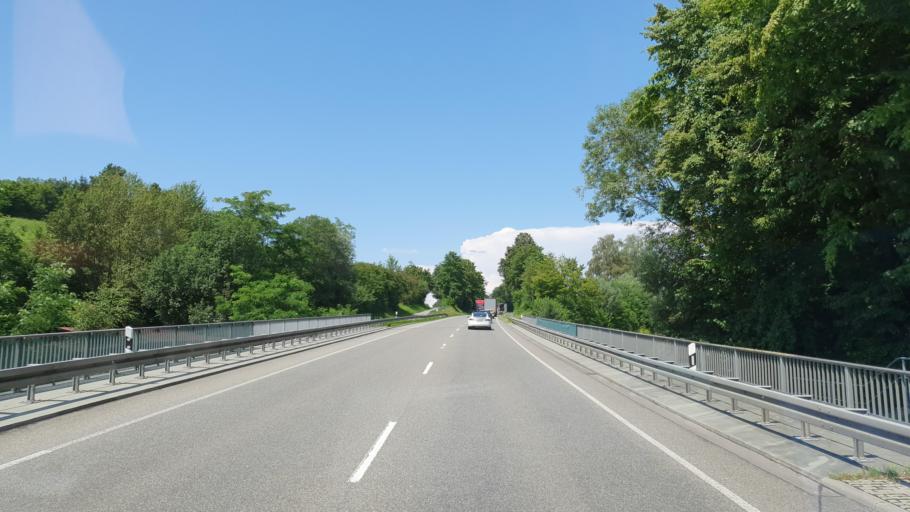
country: DE
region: Baden-Wuerttemberg
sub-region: Tuebingen Region
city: Meersburg
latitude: 47.7033
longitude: 9.2688
